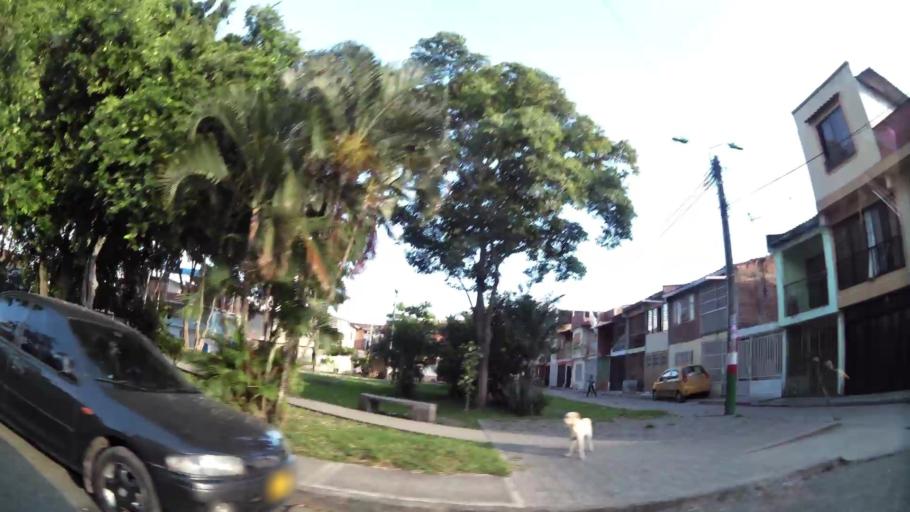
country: CO
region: Valle del Cauca
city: Cali
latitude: 3.4070
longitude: -76.5003
